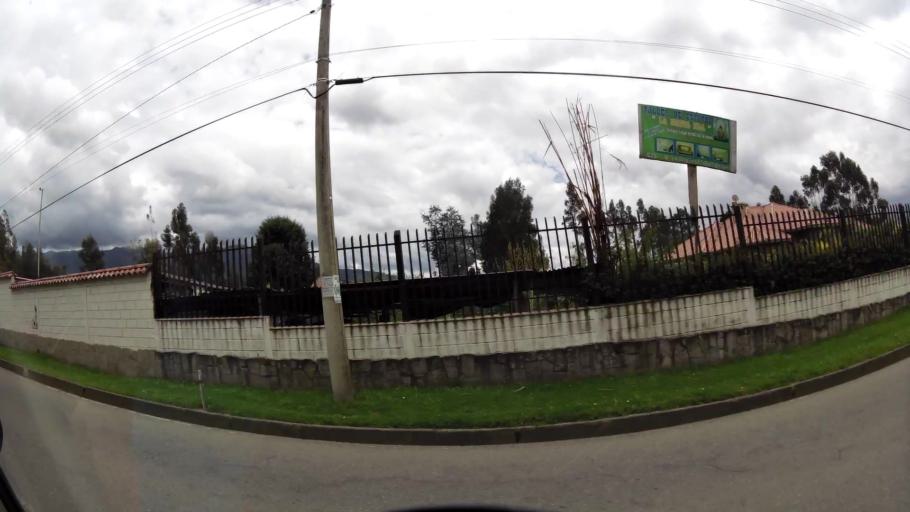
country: EC
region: Azuay
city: Cuenca
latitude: -2.8894
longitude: -79.0616
